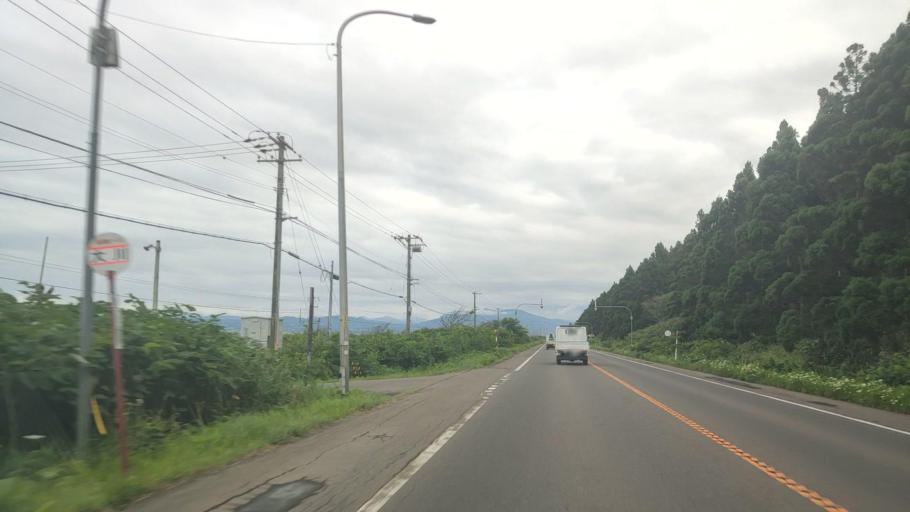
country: JP
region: Hokkaido
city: Niseko Town
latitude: 42.3415
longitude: 140.2809
